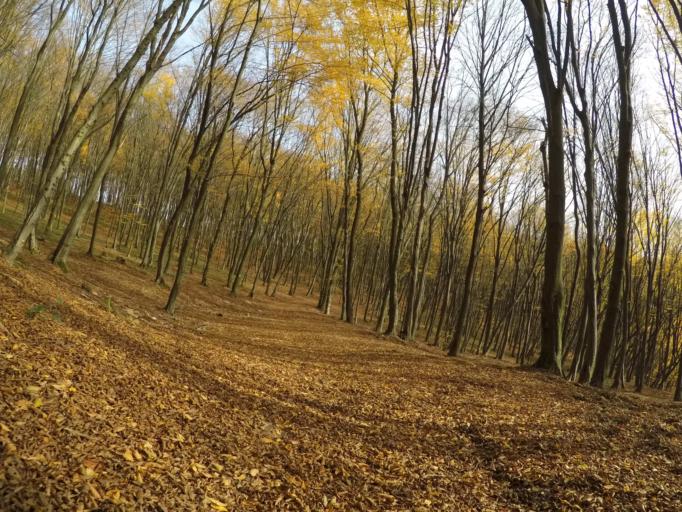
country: SK
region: Presovsky
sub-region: Okres Presov
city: Presov
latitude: 48.9202
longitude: 21.2217
